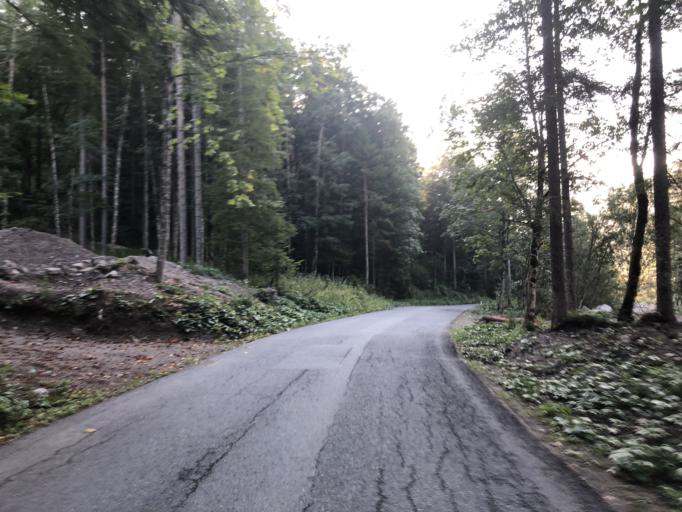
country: AT
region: Tyrol
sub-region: Politischer Bezirk Kitzbuhel
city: Schwendt
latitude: 47.5822
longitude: 12.3603
